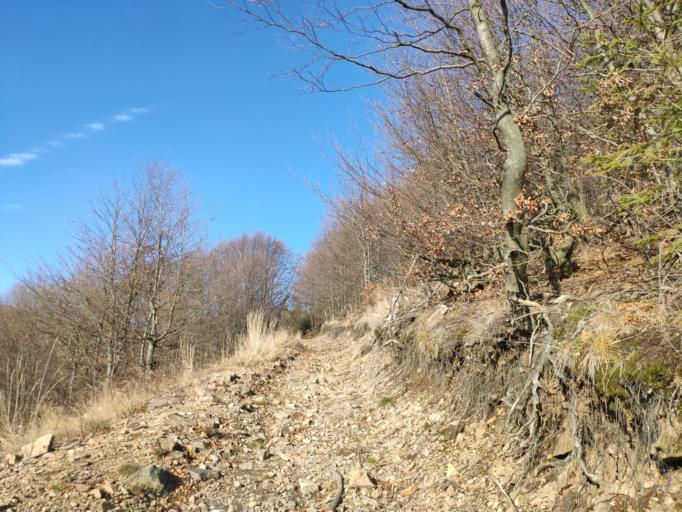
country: SK
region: Kosicky
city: Dobsina
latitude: 48.8174
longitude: 20.4682
